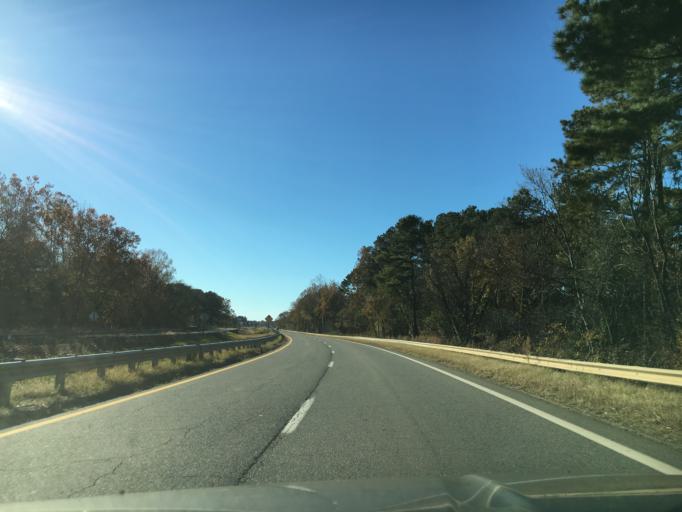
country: US
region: Virginia
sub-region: Halifax County
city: South Boston
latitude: 36.6899
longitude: -78.8717
